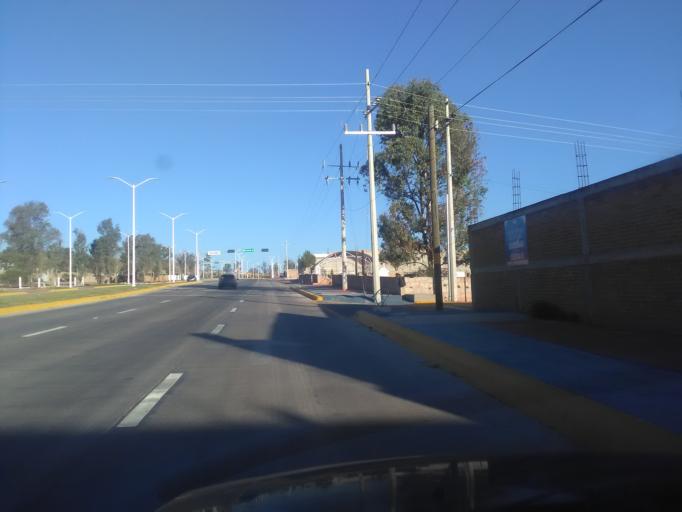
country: MX
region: Durango
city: Victoria de Durango
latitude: 23.9939
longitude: -104.7163
